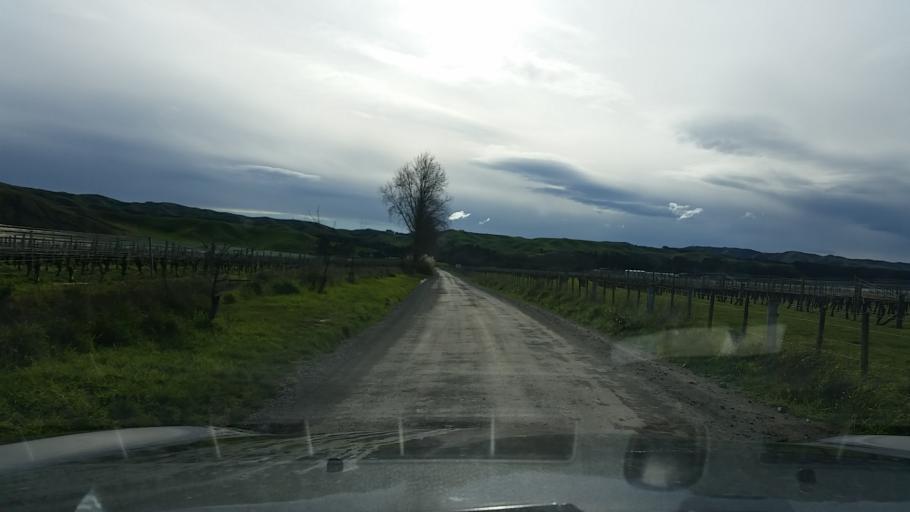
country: NZ
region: Marlborough
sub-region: Marlborough District
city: Blenheim
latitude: -41.6271
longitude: 174.1006
